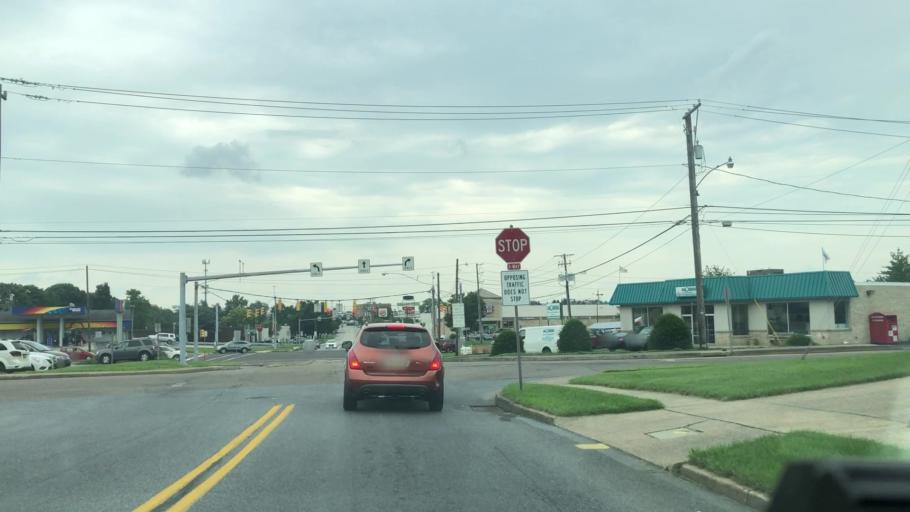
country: US
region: Pennsylvania
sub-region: Dauphin County
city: Progress
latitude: 40.2802
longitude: -76.8134
